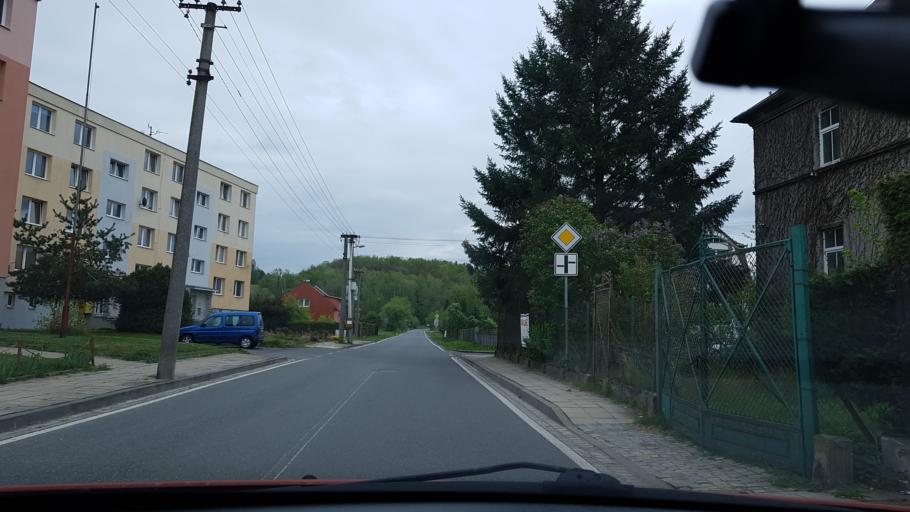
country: CZ
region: Olomoucky
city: Vidnava
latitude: 50.3713
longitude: 17.1885
